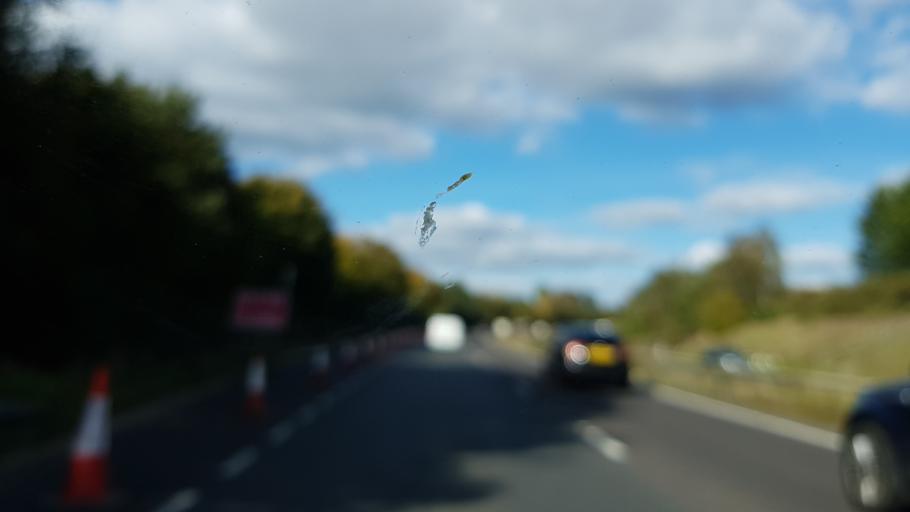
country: GB
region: England
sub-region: Surrey
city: Milford
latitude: 51.2086
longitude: -0.6508
